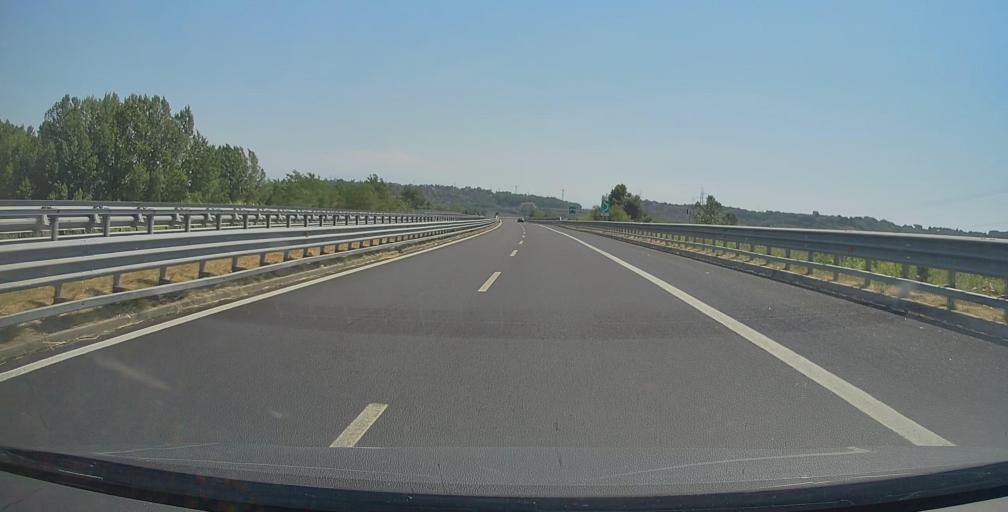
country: IT
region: Calabria
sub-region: Provincia di Reggio Calabria
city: Rosarno
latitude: 38.4934
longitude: 16.0109
